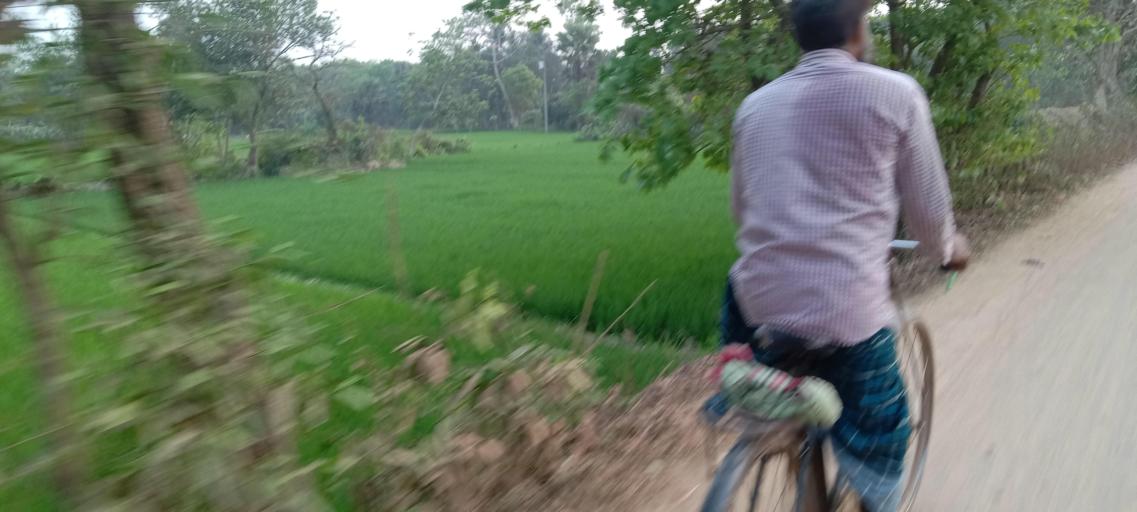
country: BD
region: Dhaka
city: Sakhipur
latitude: 24.4263
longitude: 90.2622
